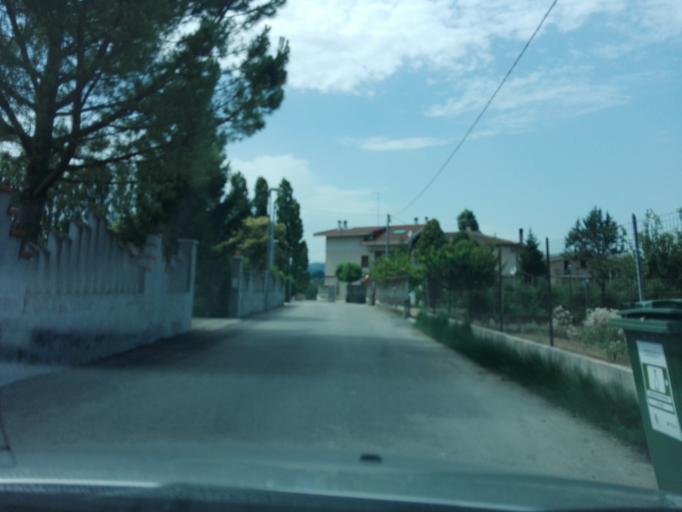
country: IT
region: Abruzzo
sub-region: Provincia di Pescara
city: Cappelle sul Tavo
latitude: 42.4905
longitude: 14.1187
